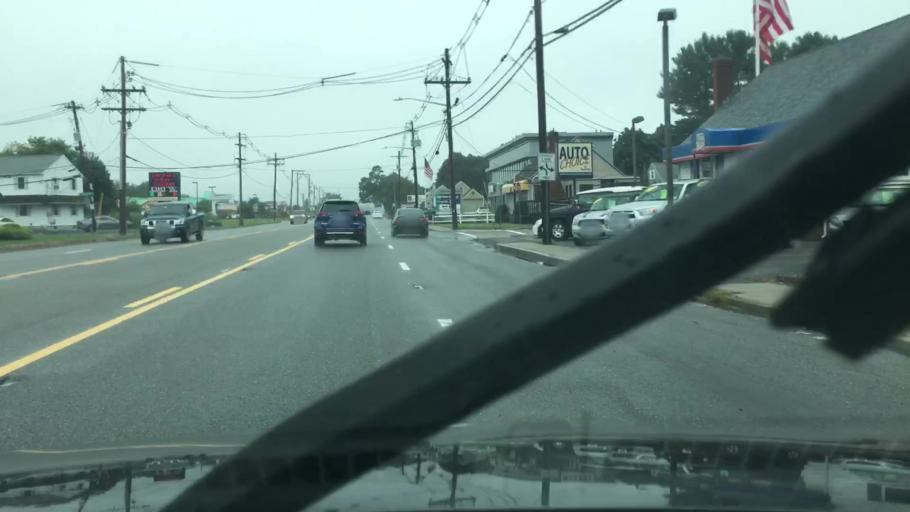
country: US
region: Massachusetts
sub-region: Essex County
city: Peabody
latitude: 42.5487
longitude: -70.9516
